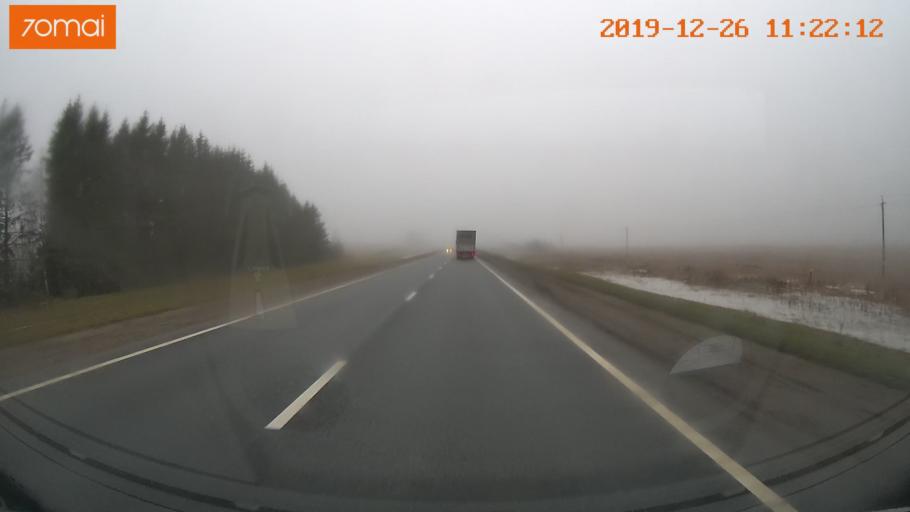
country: RU
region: Vologda
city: Chebsara
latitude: 59.1272
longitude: 38.9487
